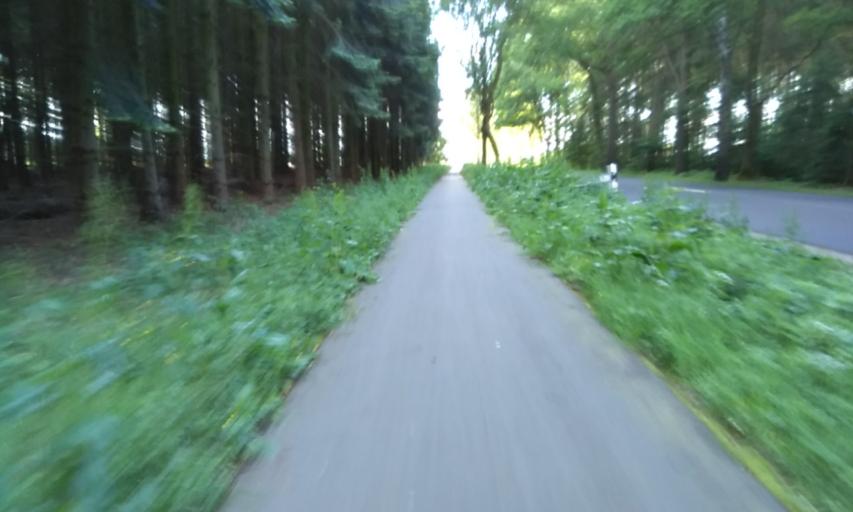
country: DE
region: Lower Saxony
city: Anderlingen
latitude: 53.3640
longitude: 9.3035
